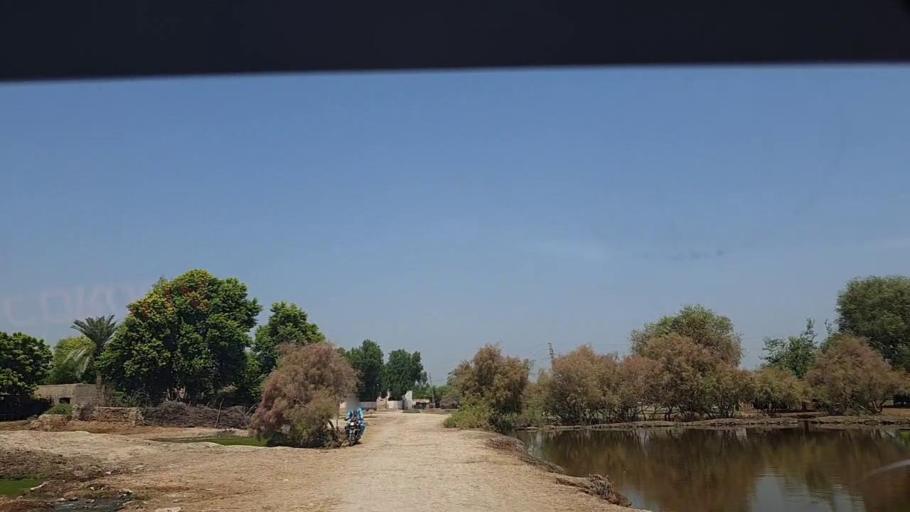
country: PK
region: Sindh
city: Ghauspur
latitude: 28.1872
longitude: 69.0886
